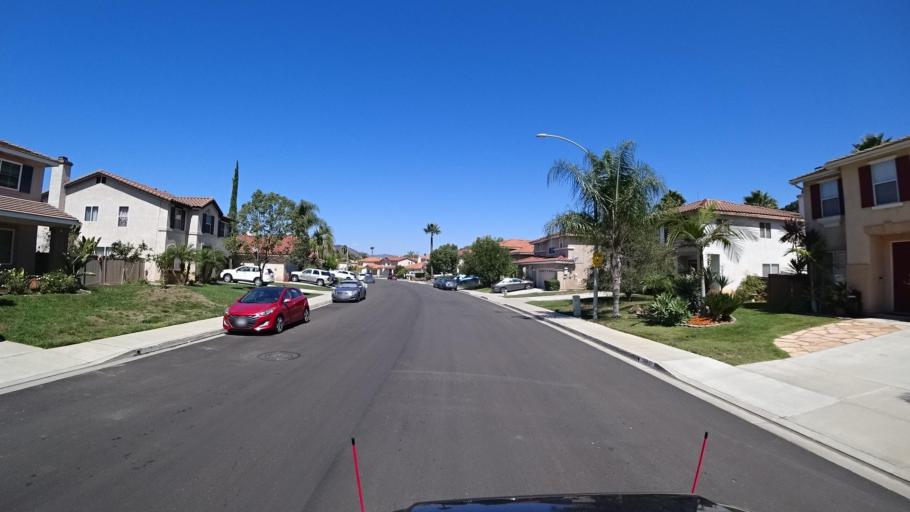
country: US
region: California
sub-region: San Diego County
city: Rainbow
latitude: 33.3257
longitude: -117.1487
